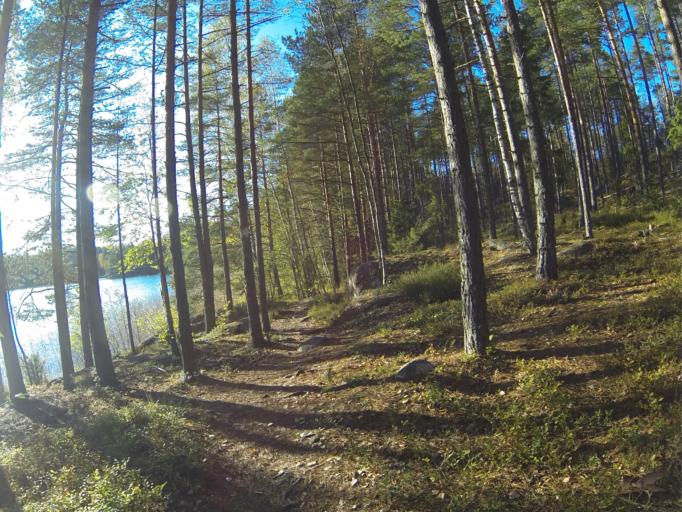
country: FI
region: Varsinais-Suomi
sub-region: Salo
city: Saerkisalo
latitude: 60.2159
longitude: 22.9249
